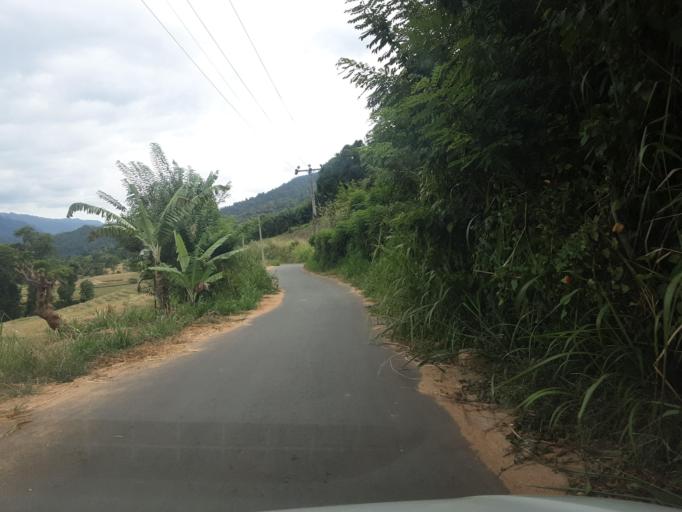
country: LK
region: Uva
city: Badulla
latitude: 7.0912
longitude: 80.9393
